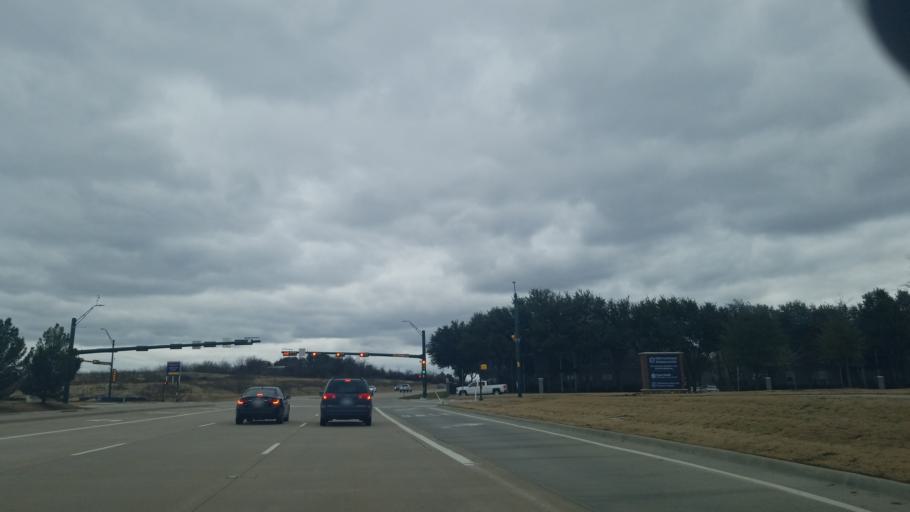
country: US
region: Texas
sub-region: Denton County
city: Double Oak
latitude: 33.0543
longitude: -97.0748
